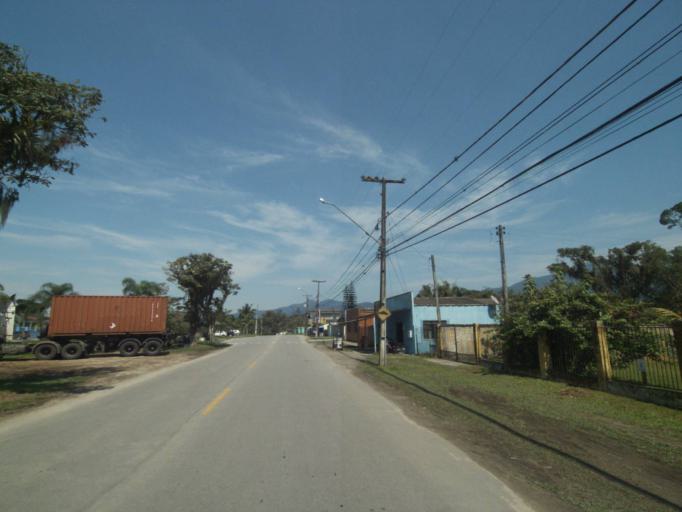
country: BR
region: Parana
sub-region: Paranagua
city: Paranagua
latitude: -25.5564
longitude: -48.6273
